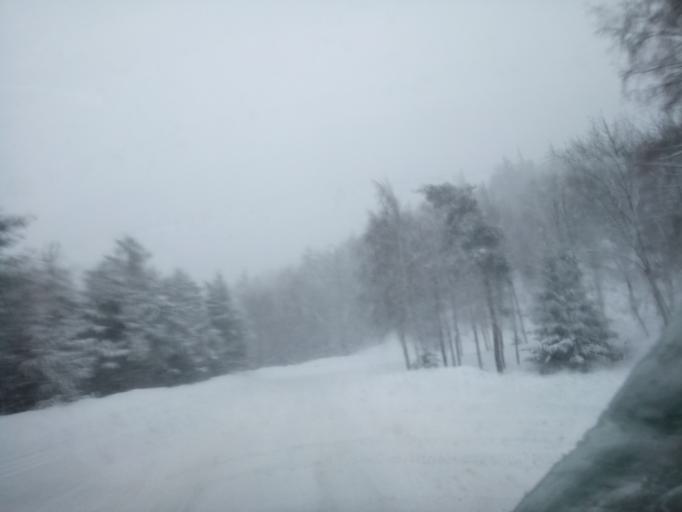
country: FR
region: Rhone-Alpes
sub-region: Departement de la Savoie
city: Modane
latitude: 45.2034
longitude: 6.7007
